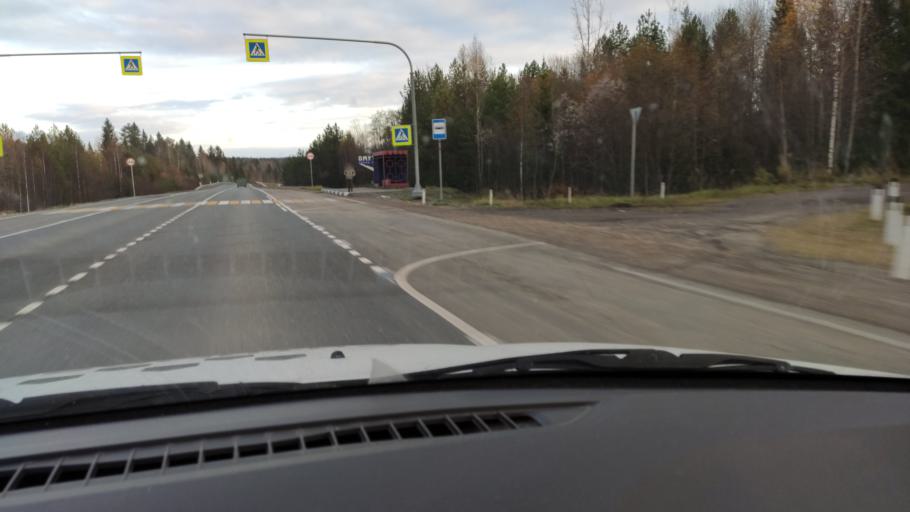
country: RU
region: Kirov
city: Omutninsk
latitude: 58.6975
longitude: 52.1227
